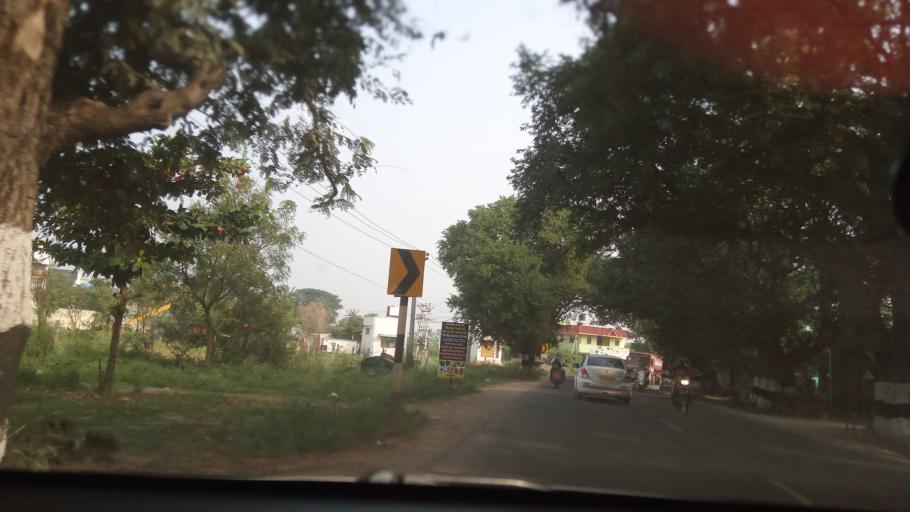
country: IN
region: Tamil Nadu
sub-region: Coimbatore
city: Periyanayakkanpalaiyam
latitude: 11.1441
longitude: 77.0413
